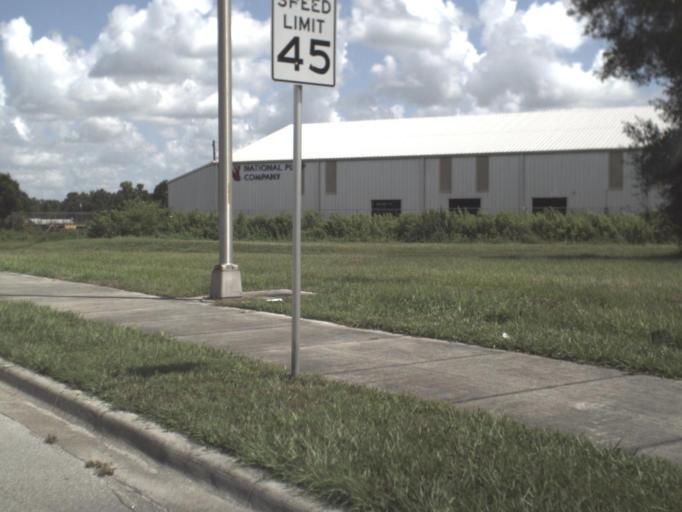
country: US
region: Florida
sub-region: Hardee County
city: Zolfo Springs
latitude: 27.4968
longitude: -81.7963
